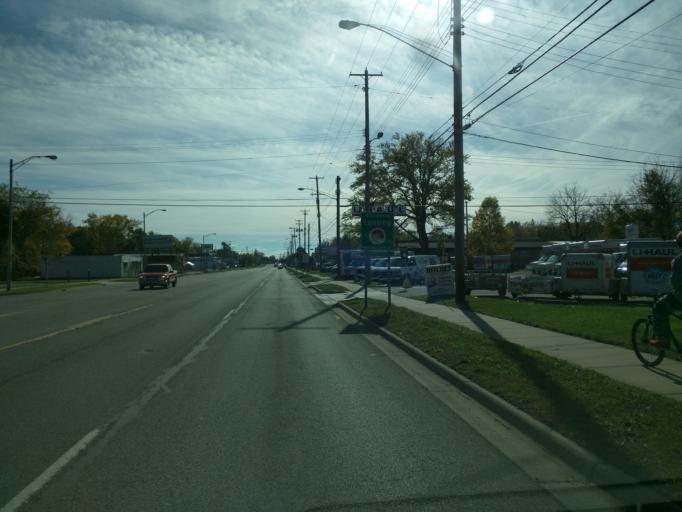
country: US
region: Michigan
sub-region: Ingham County
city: Lansing
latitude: 42.7690
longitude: -84.5428
